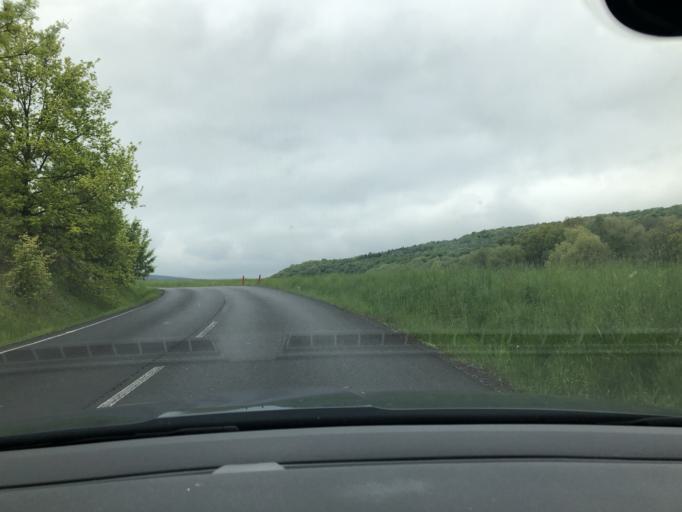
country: CZ
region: Ustecky
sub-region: Okres Usti nad Labem
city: Usti nad Labem
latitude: 50.7087
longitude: 14.0140
